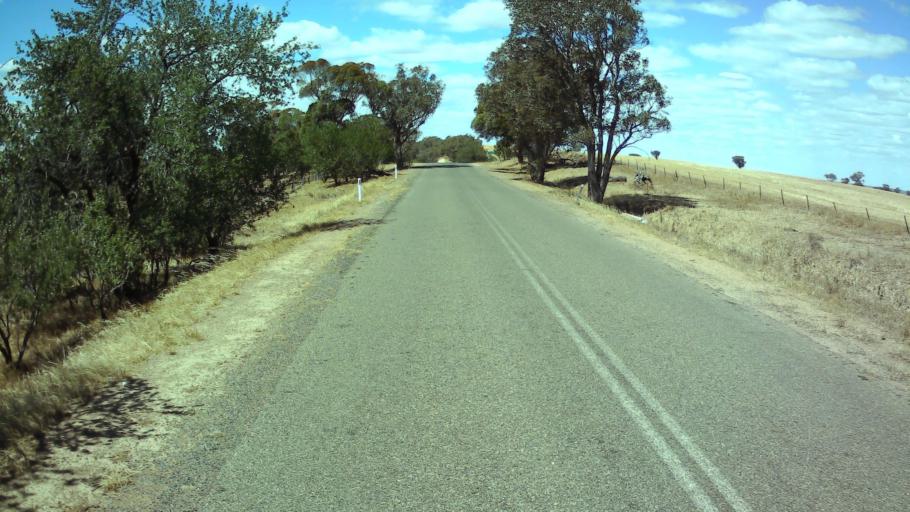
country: AU
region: New South Wales
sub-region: Young
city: Young
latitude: -34.1177
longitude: 148.3903
